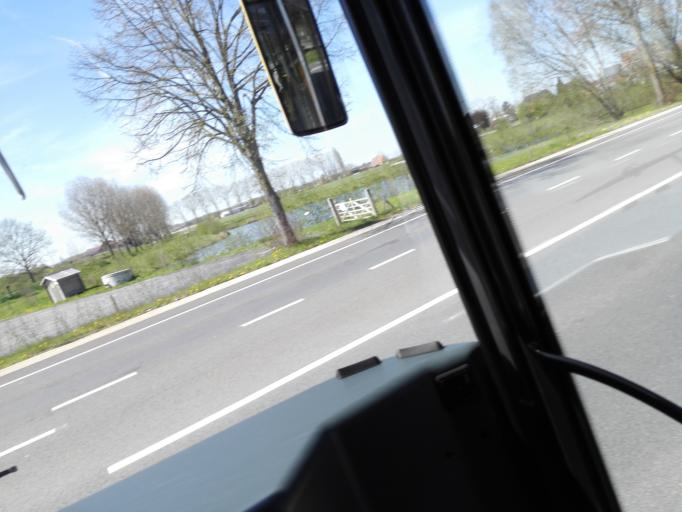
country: BE
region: Flanders
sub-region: Provincie West-Vlaanderen
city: Meulebeke
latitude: 50.9471
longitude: 3.2760
